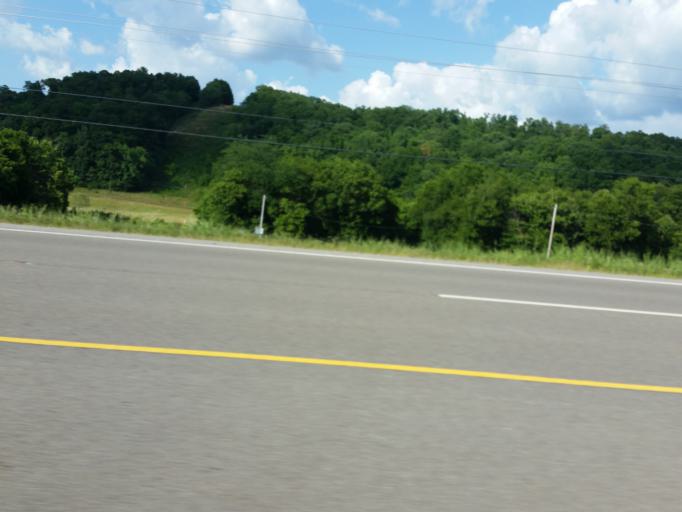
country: US
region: Tennessee
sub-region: Lewis County
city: Hohenwald
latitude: 35.5746
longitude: -87.4273
